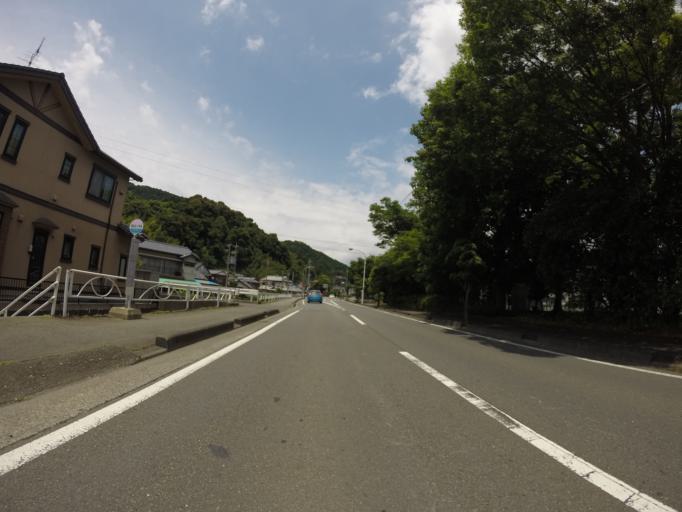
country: JP
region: Shizuoka
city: Shizuoka-shi
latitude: 34.9611
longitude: 138.3585
